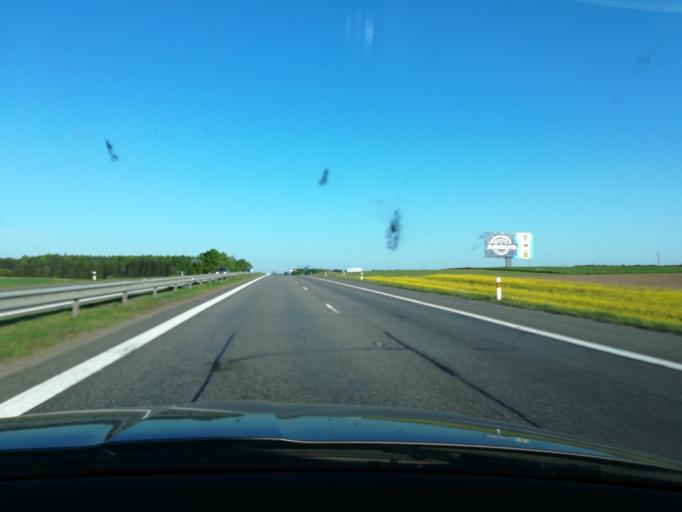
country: LT
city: Kaisiadorys
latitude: 54.8469
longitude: 24.3249
